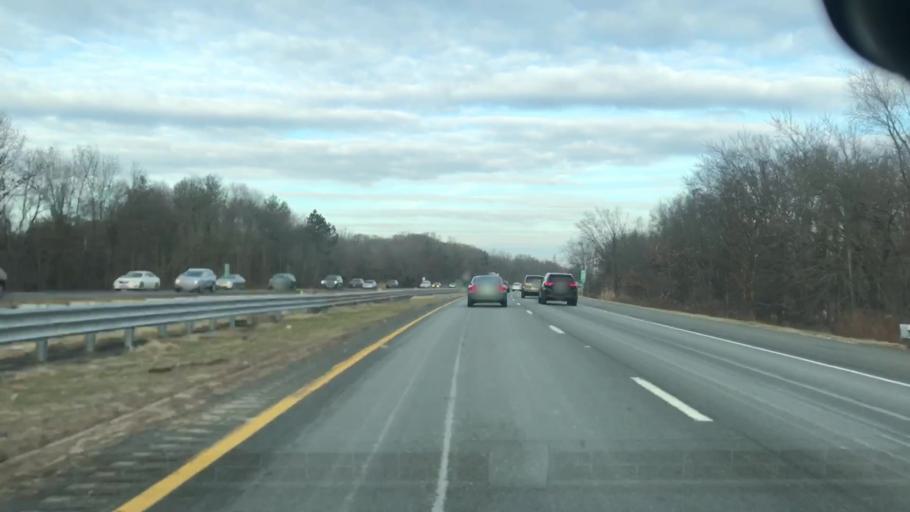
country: US
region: New Jersey
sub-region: Essex County
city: West Caldwell
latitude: 40.8330
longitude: -74.3330
